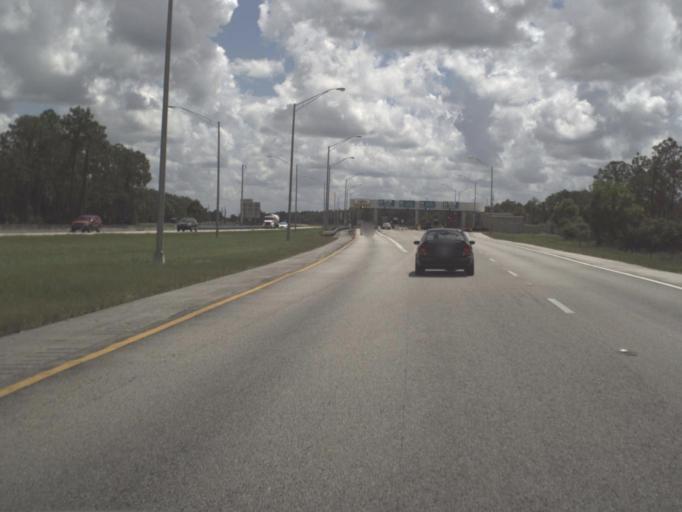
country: US
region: Florida
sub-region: Collier County
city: Golden Gate
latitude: 26.1561
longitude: -81.6713
